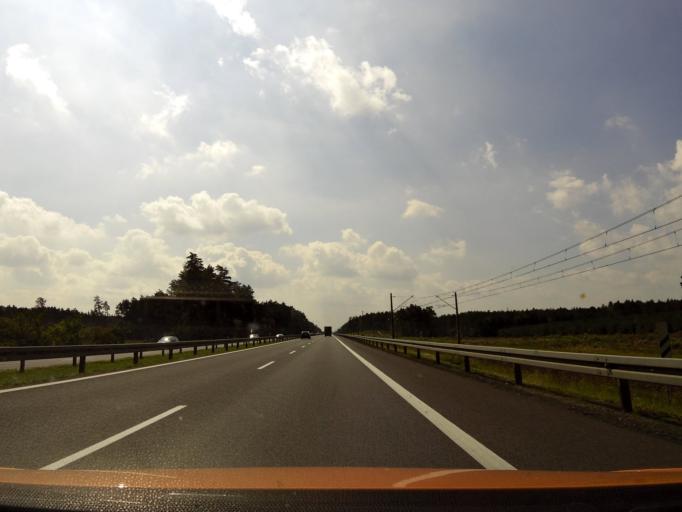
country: PL
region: West Pomeranian Voivodeship
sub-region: Powiat goleniowski
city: Goleniow
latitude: 53.5114
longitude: 14.8027
